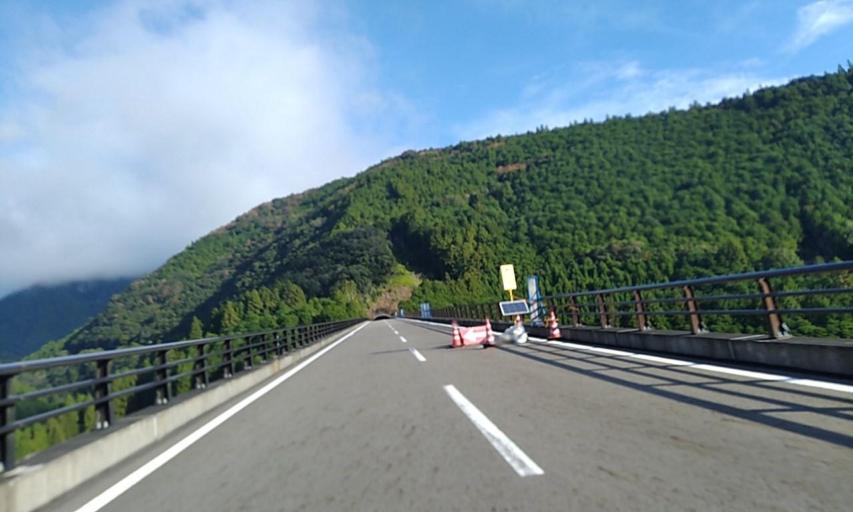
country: JP
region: Wakayama
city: Shingu
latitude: 33.8929
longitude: 135.8798
